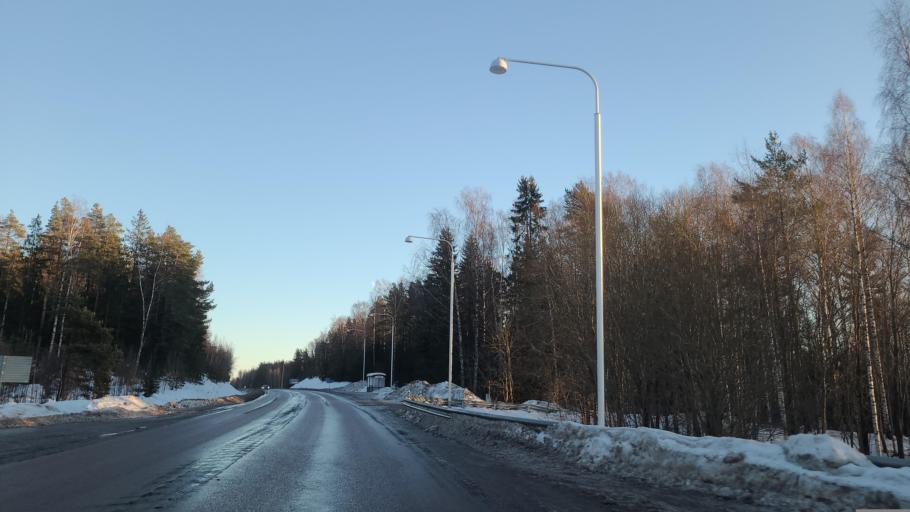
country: SE
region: Gaevleborg
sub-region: Soderhamns Kommun
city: Soderhamn
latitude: 61.2865
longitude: 16.9633
